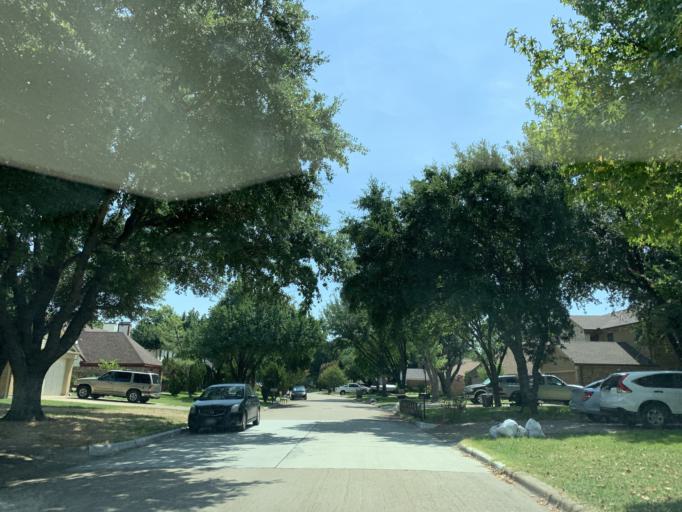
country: US
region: Texas
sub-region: Dallas County
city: Grand Prairie
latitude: 32.6654
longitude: -97.0399
